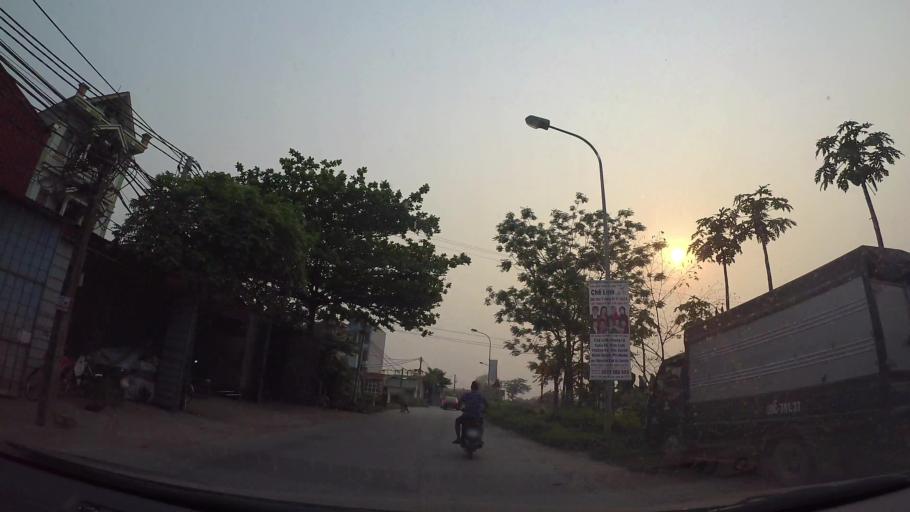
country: VN
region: Ha Noi
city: Kim Bai
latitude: 20.8686
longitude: 105.8128
